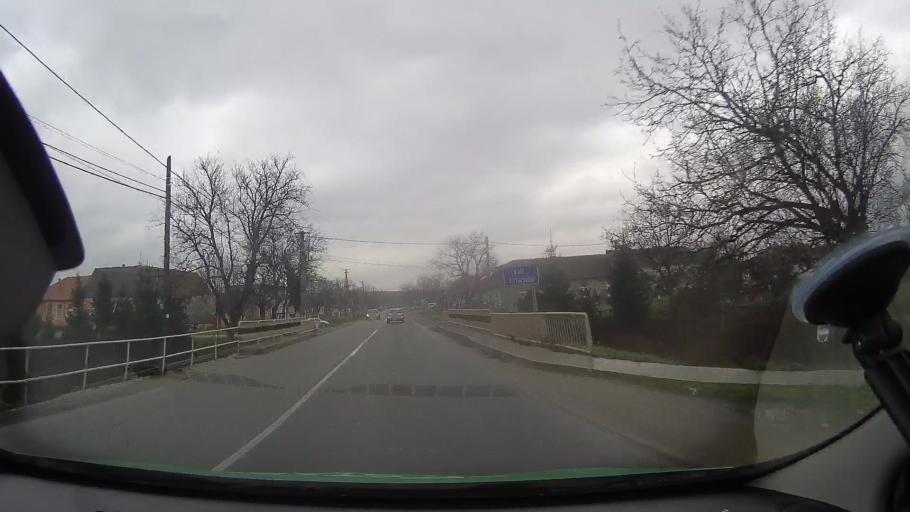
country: RO
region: Arad
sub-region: Comuna Almas
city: Almas
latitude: 46.2844
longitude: 22.2362
